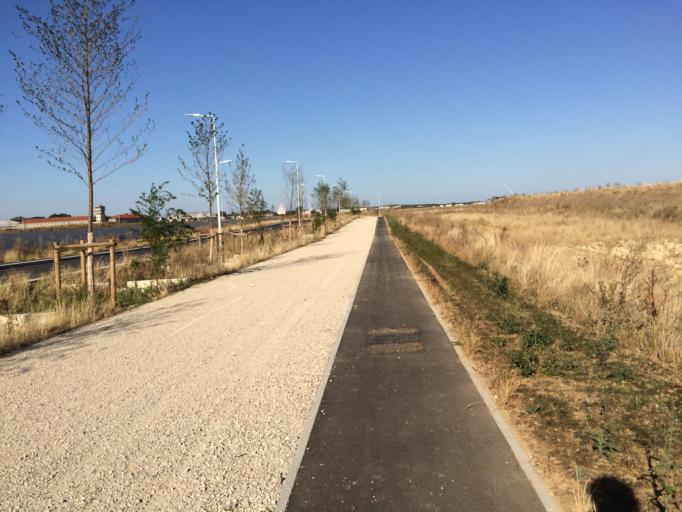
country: FR
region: Ile-de-France
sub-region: Departement de l'Essonne
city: Le Plessis-Pate
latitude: 48.5958
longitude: 2.3225
